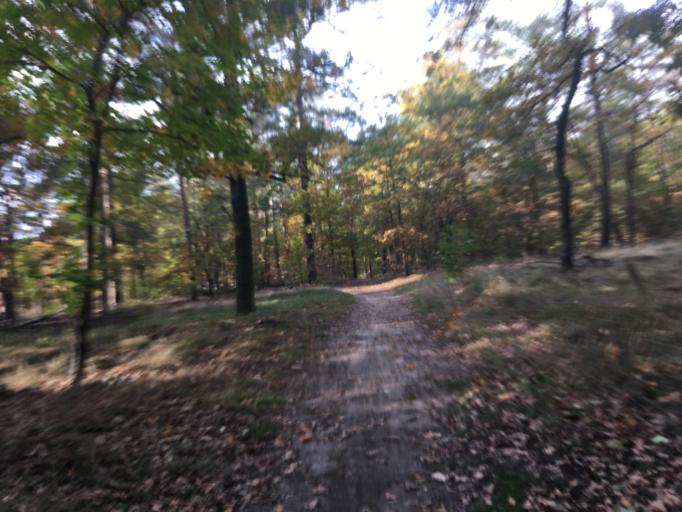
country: DE
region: Berlin
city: Kopenick Bezirk
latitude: 52.4671
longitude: 13.5588
